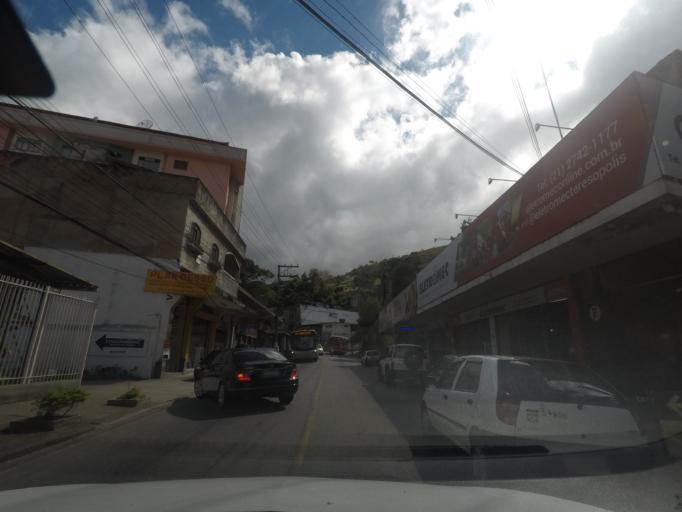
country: BR
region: Rio de Janeiro
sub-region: Teresopolis
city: Teresopolis
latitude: -22.3999
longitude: -42.9616
